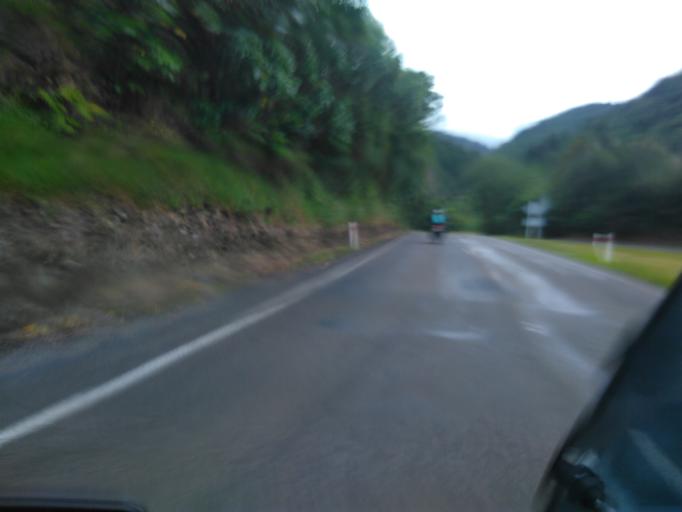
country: NZ
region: Bay of Plenty
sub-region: Opotiki District
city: Opotiki
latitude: -38.3028
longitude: 177.3961
